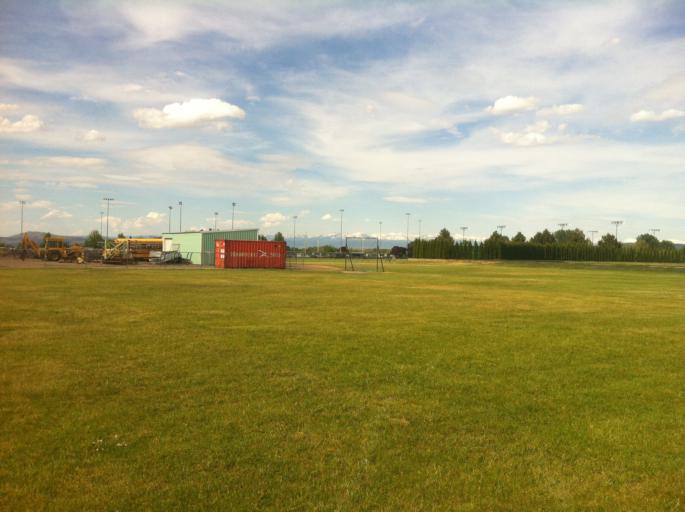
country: US
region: Oregon
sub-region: Baker County
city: Baker City
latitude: 44.7884
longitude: -117.8378
